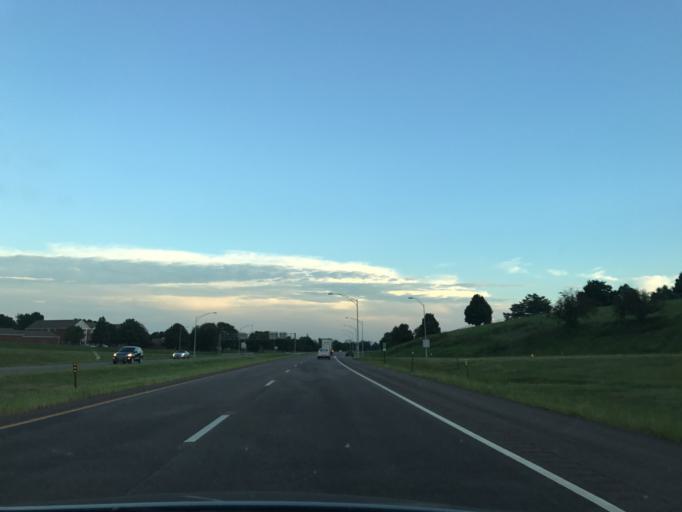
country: US
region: Nebraska
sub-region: Lancaster County
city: Lincoln
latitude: 40.8547
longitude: -96.7130
